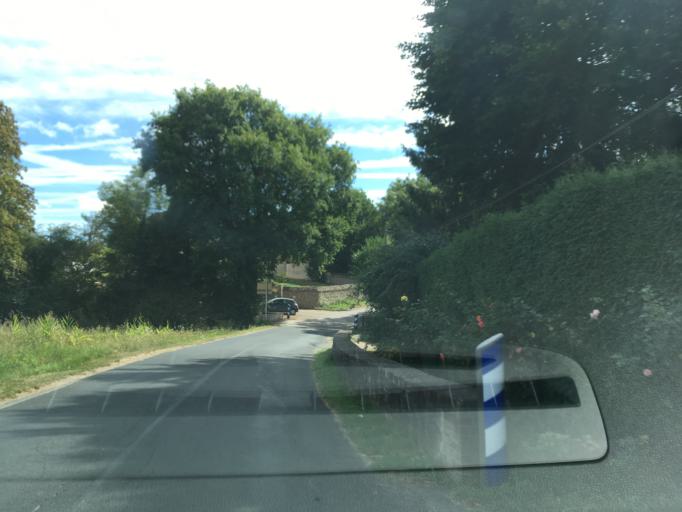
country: FR
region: Haute-Normandie
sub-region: Departement de l'Eure
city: Saint-Aubin-sur-Gaillon
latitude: 49.1381
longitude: 1.2988
